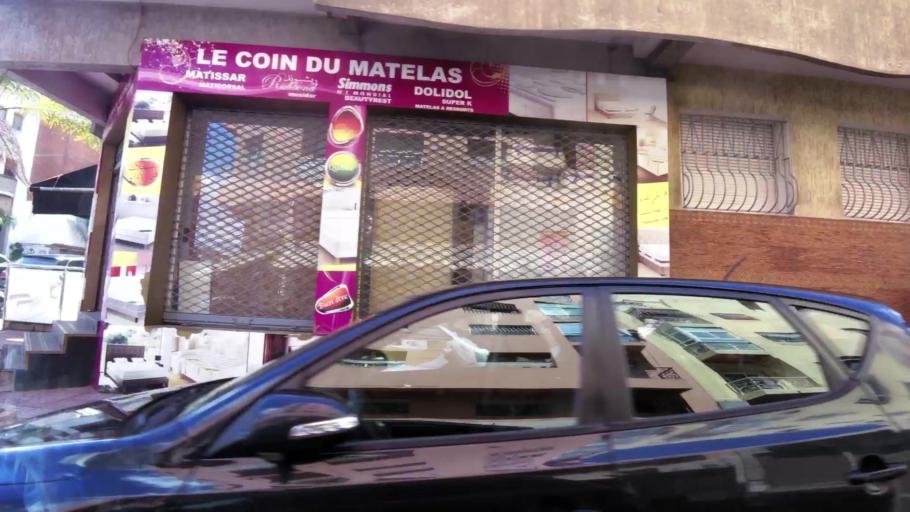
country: MA
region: Grand Casablanca
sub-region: Casablanca
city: Casablanca
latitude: 33.5591
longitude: -7.6752
